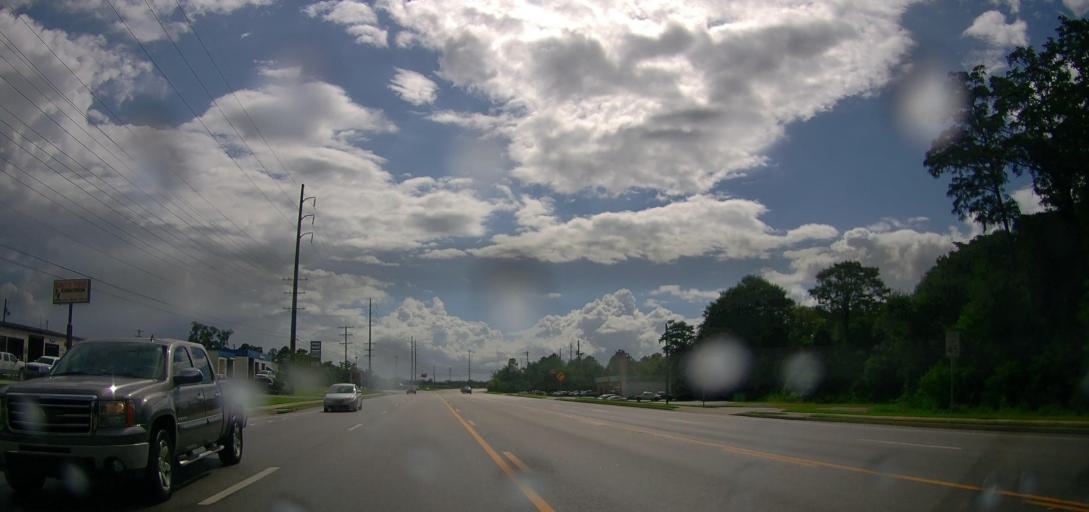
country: US
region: Georgia
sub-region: Coffee County
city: Douglas
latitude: 31.4898
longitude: -82.8371
